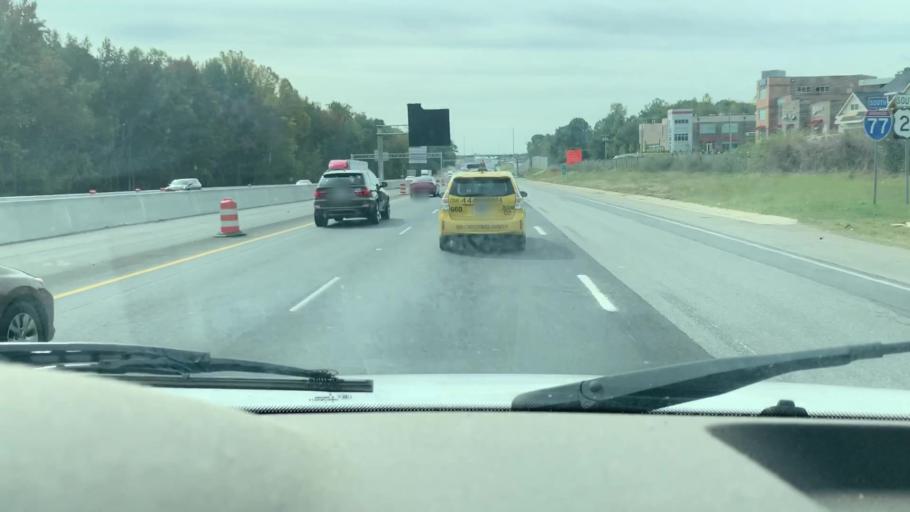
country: US
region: North Carolina
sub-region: Gaston County
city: Davidson
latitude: 35.5437
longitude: -80.8596
